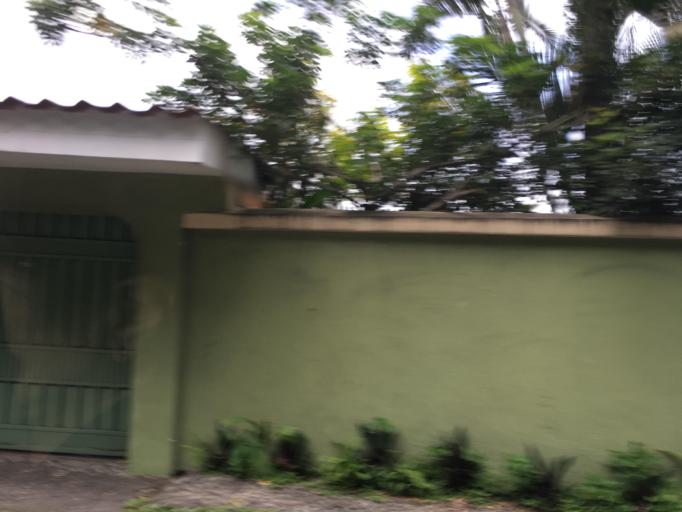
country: GT
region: Guatemala
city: Villa Canales
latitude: 14.4376
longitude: -90.5356
